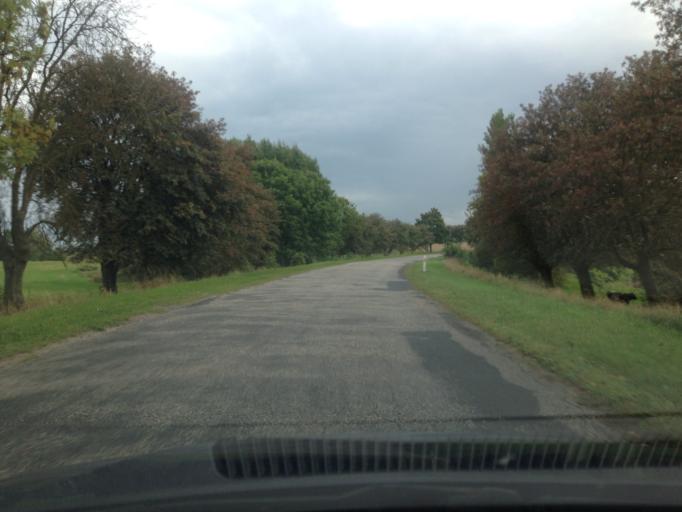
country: PL
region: Kujawsko-Pomorskie
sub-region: Powiat lipnowski
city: Lipno
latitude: 52.7951
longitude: 19.2074
